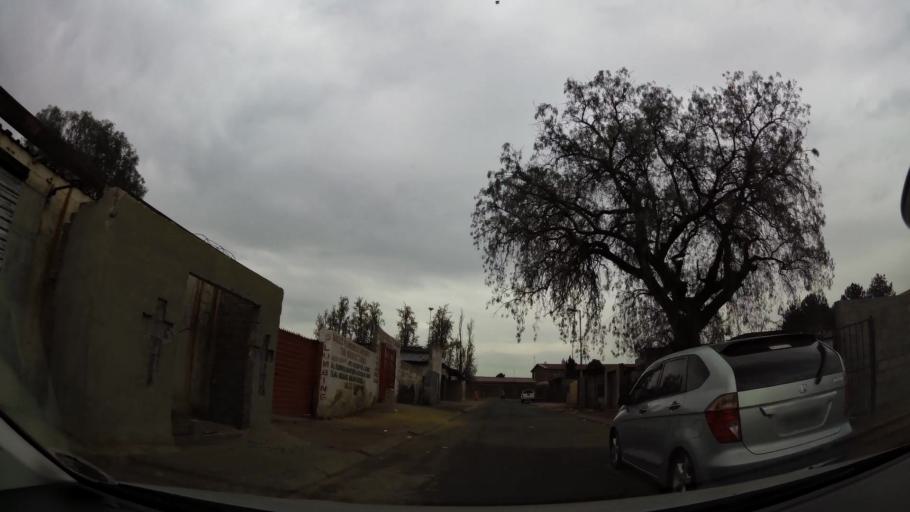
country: ZA
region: Gauteng
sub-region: City of Johannesburg Metropolitan Municipality
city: Soweto
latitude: -26.2523
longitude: 27.8725
